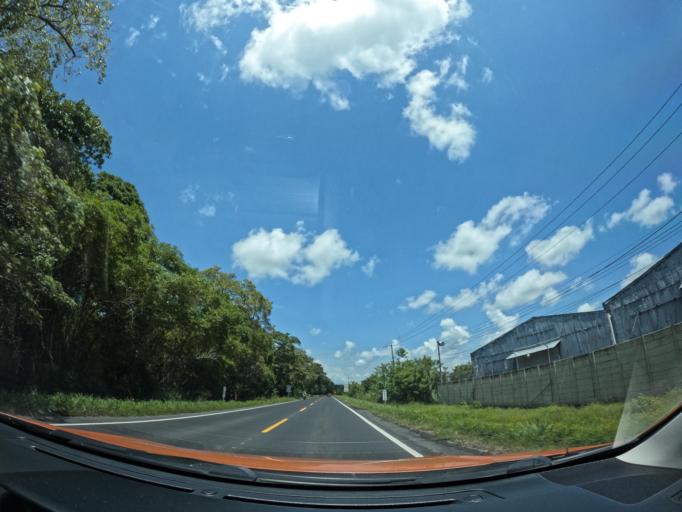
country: GT
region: Escuintla
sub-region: Municipio de Masagua
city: Masagua
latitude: 14.1650
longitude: -90.8792
